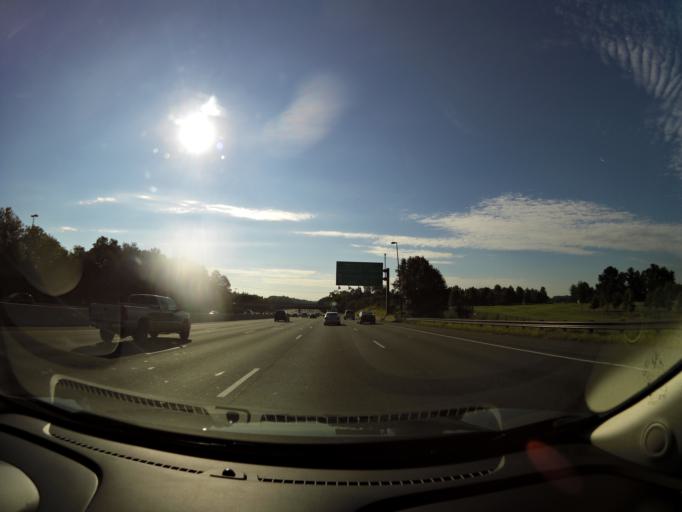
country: US
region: Maryland
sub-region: Montgomery County
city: Gaithersburg
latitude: 39.1338
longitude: -77.2087
